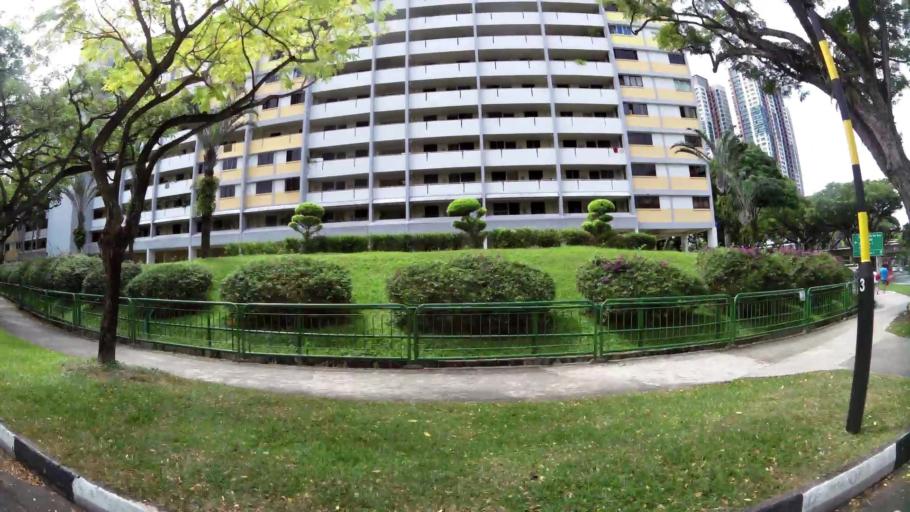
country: SG
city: Singapore
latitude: 1.3169
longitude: 103.7660
